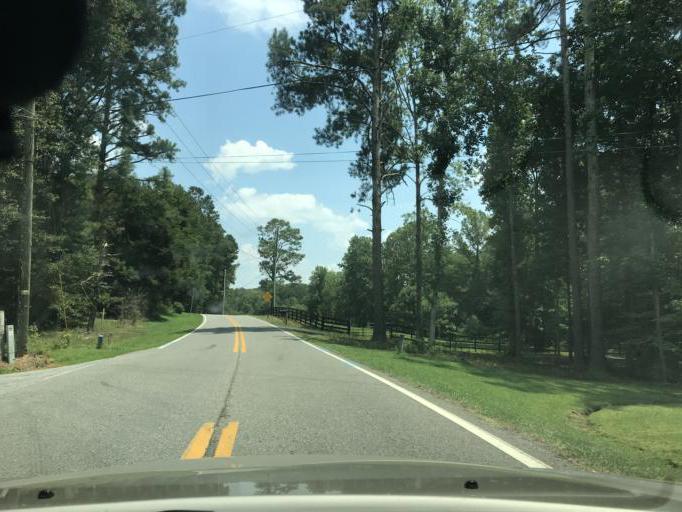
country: US
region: Georgia
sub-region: Forsyth County
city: Cumming
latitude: 34.2705
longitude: -84.1605
